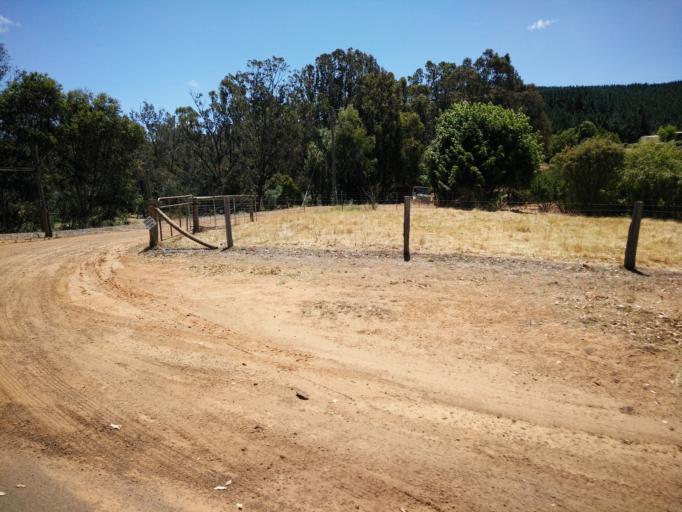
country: AU
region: Western Australia
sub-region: Bridgetown-Greenbushes
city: Bridgetown
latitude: -33.9351
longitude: 116.0274
